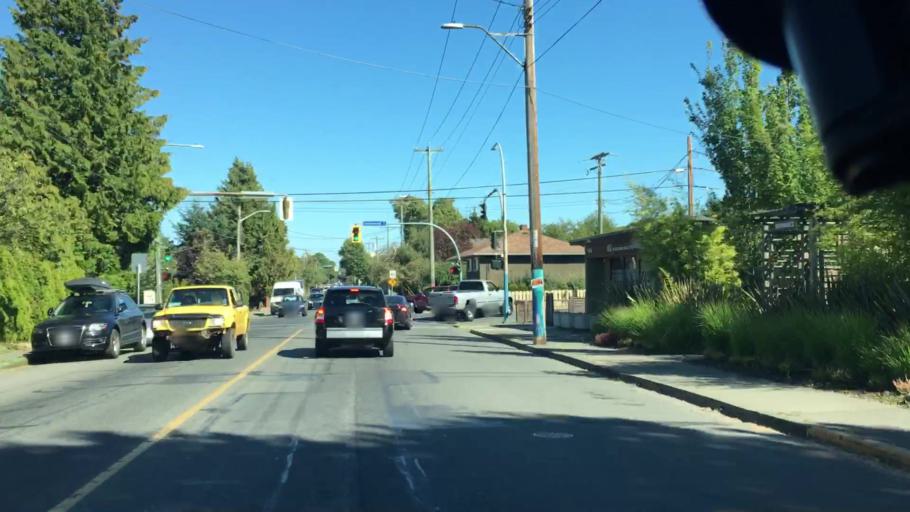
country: CA
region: British Columbia
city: Victoria
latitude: 48.4345
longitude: -123.3456
